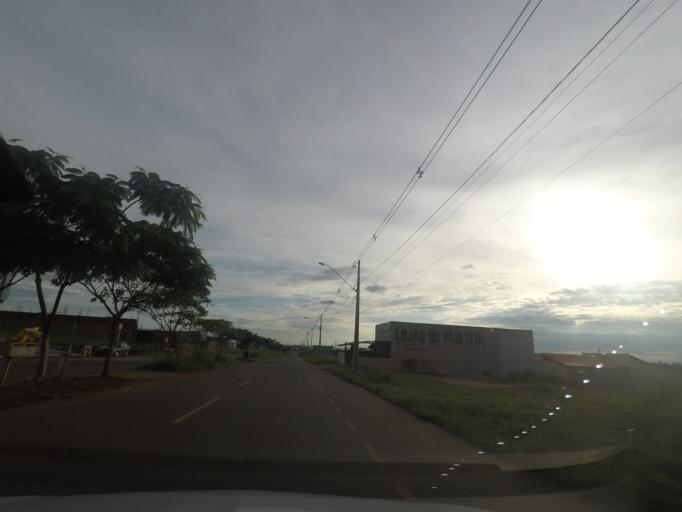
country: BR
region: Goias
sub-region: Trindade
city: Trindade
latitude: -16.7249
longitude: -49.4043
